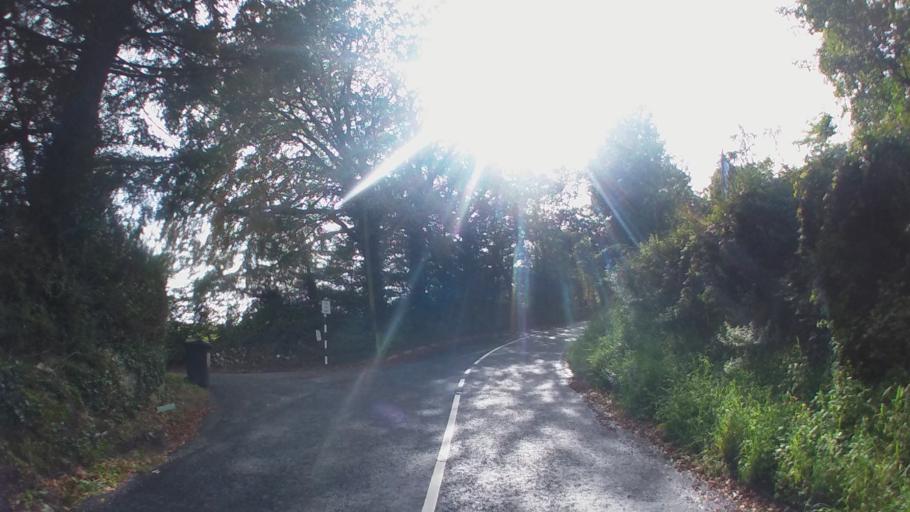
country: IE
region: Leinster
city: Sandyford
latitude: 53.2336
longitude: -6.2216
